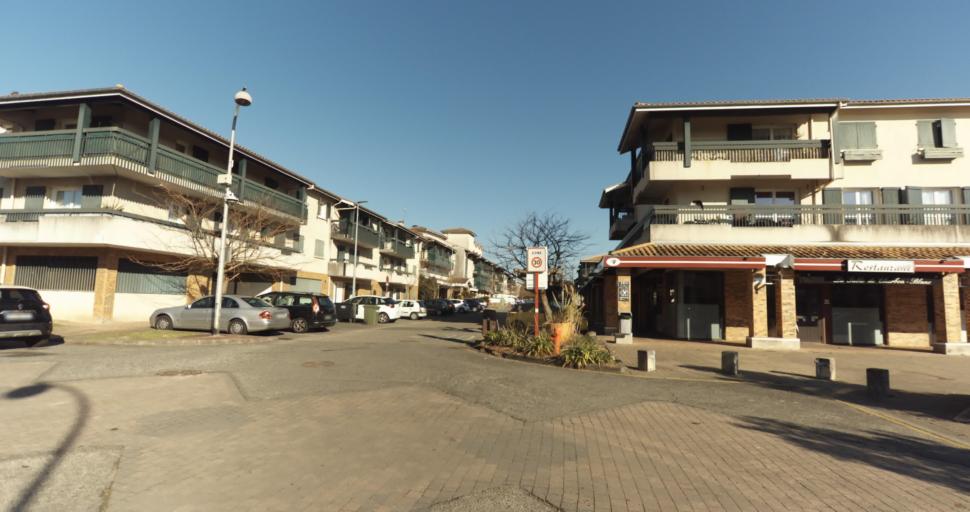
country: FR
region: Aquitaine
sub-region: Departement de la Gironde
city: Carbon-Blanc
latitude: 44.8957
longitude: -0.5021
